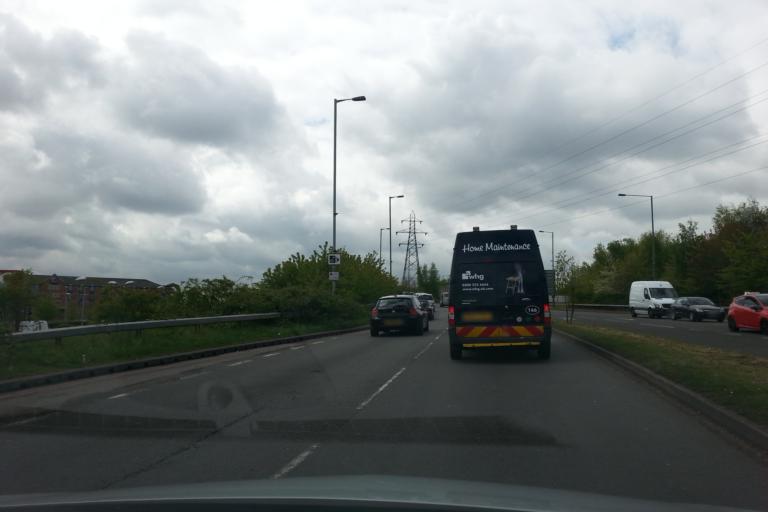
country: GB
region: England
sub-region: Walsall
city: Walsall
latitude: 52.5864
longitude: -2.0109
